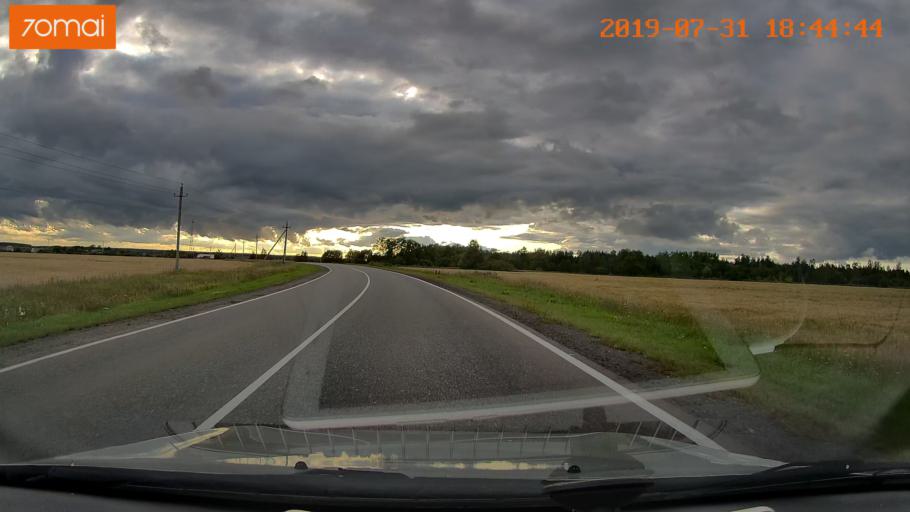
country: RU
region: Moskovskaya
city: Troitskoye
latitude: 55.2518
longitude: 38.5457
